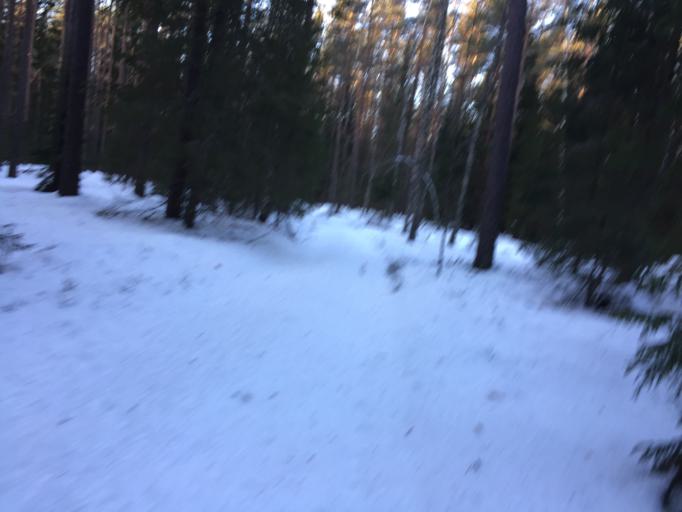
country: LV
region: Kegums
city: Kegums
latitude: 56.7322
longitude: 24.6450
